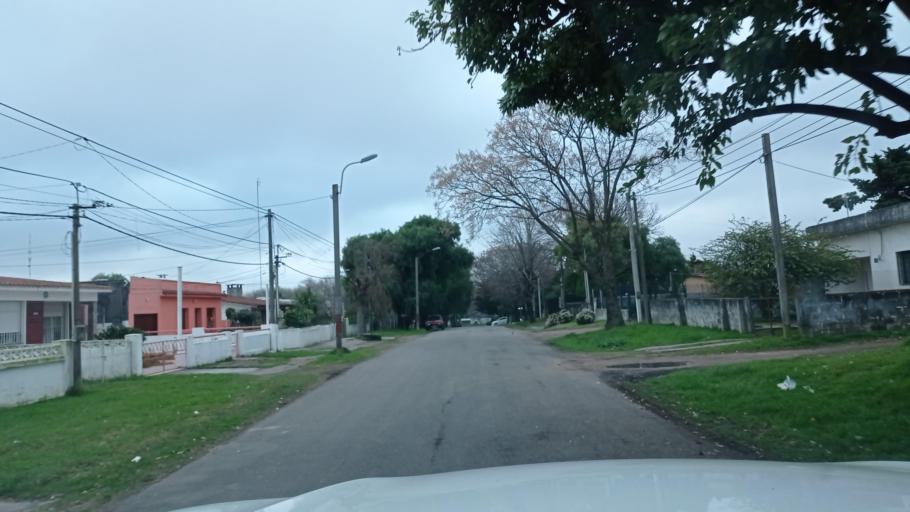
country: UY
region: Canelones
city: La Paz
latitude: -34.8362
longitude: -56.2288
